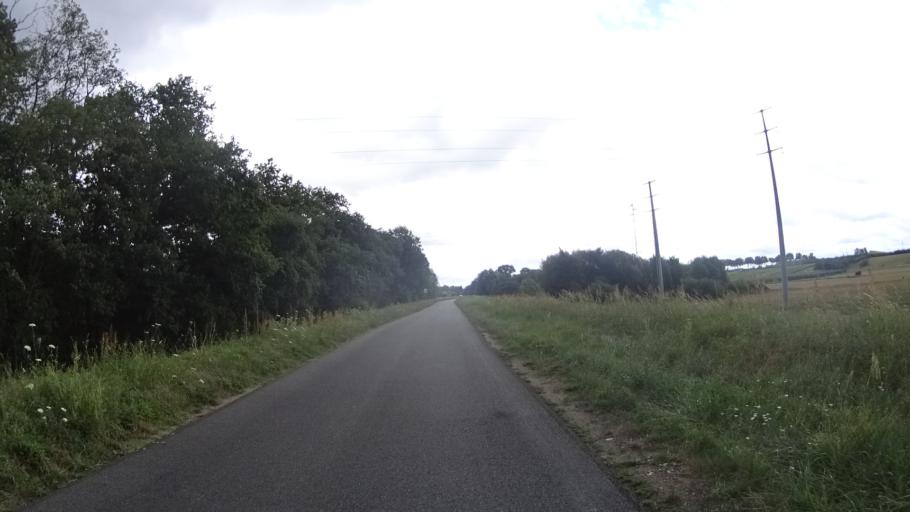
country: FR
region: Centre
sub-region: Departement du Loiret
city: Saint-Hilaire-Saint-Mesmin
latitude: 47.8632
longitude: 1.8094
